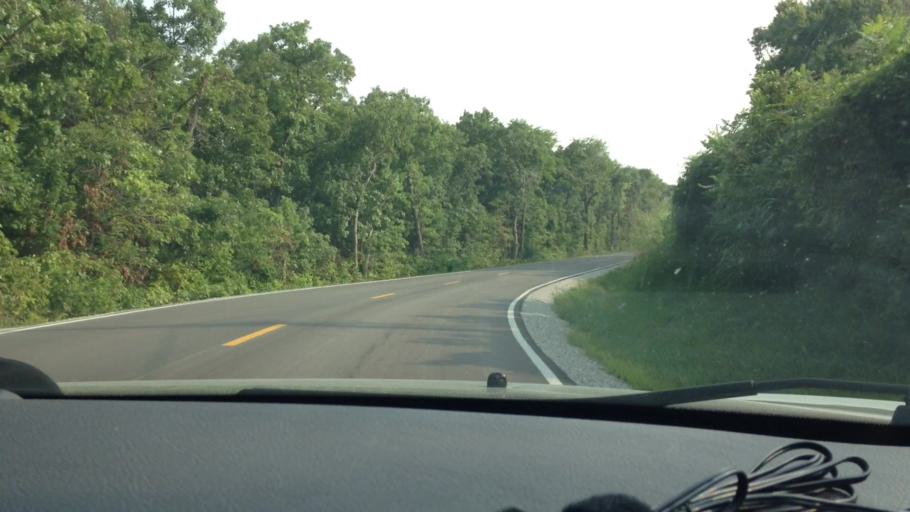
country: US
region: Missouri
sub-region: Platte County
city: Platte City
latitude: 39.3895
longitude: -94.7795
